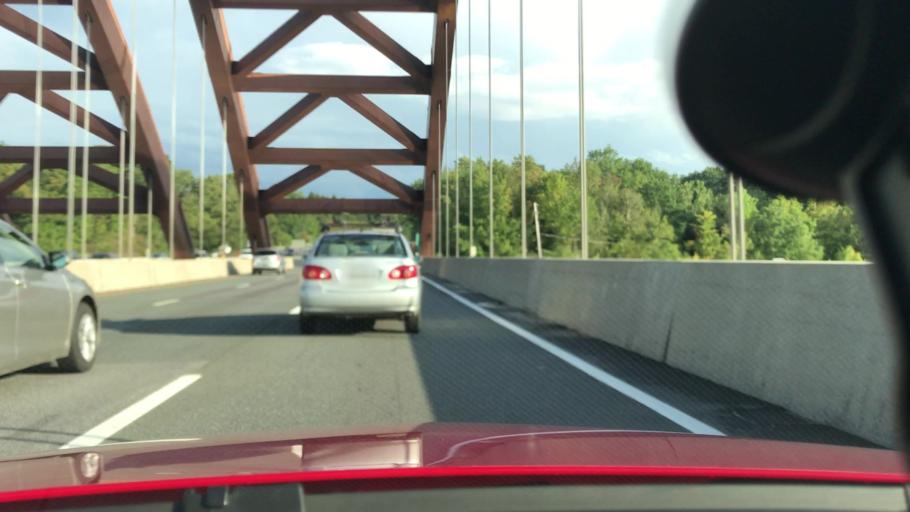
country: US
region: New York
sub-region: Albany County
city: Cohoes
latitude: 42.7915
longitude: -73.7615
